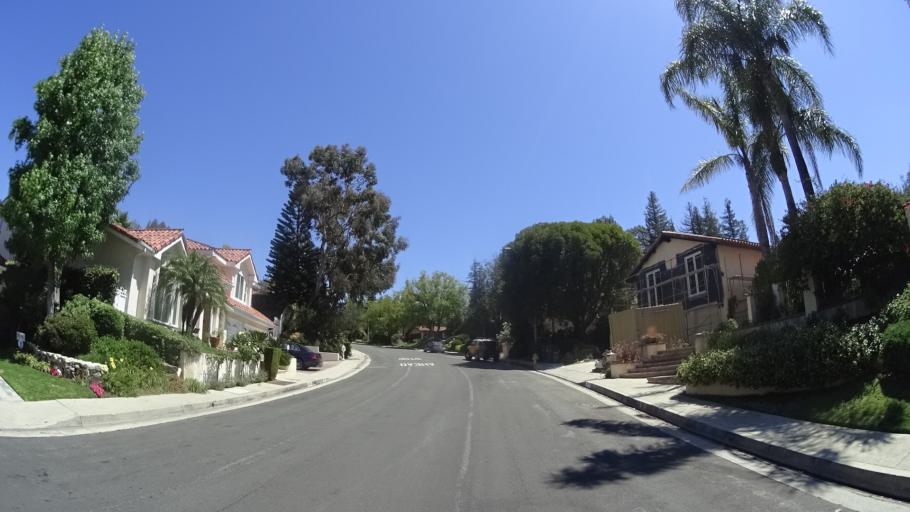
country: US
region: California
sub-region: Los Angeles County
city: Sherman Oaks
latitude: 34.1257
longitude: -118.4496
